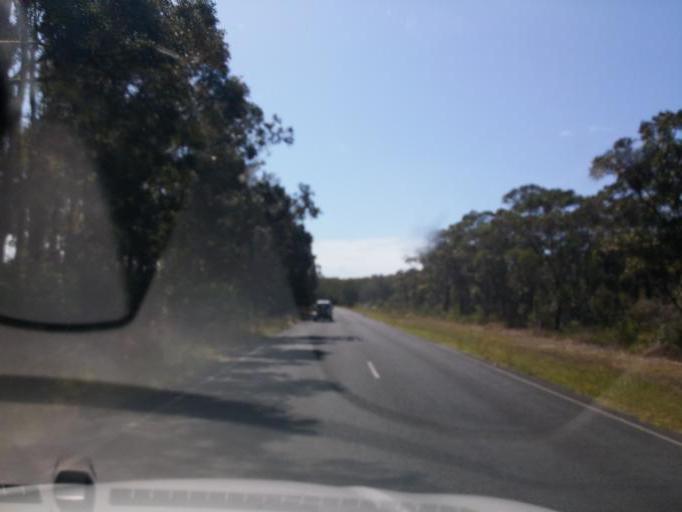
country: AU
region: New South Wales
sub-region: Great Lakes
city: Forster
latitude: -32.2355
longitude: 152.5422
